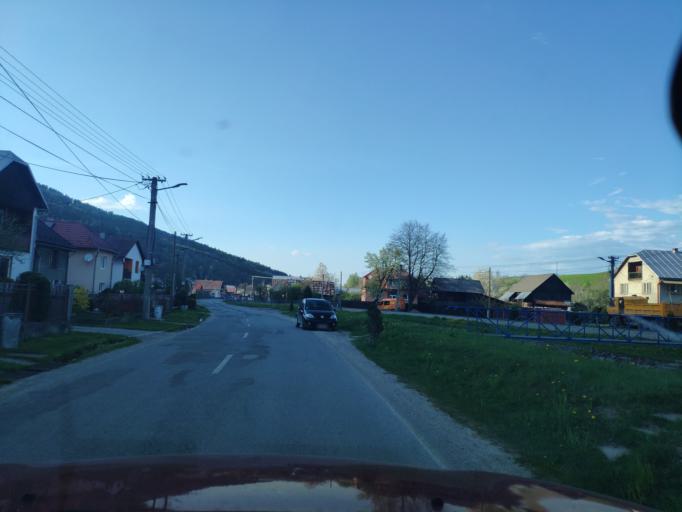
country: SK
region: Presovsky
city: Lipany
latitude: 49.0965
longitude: 20.8493
